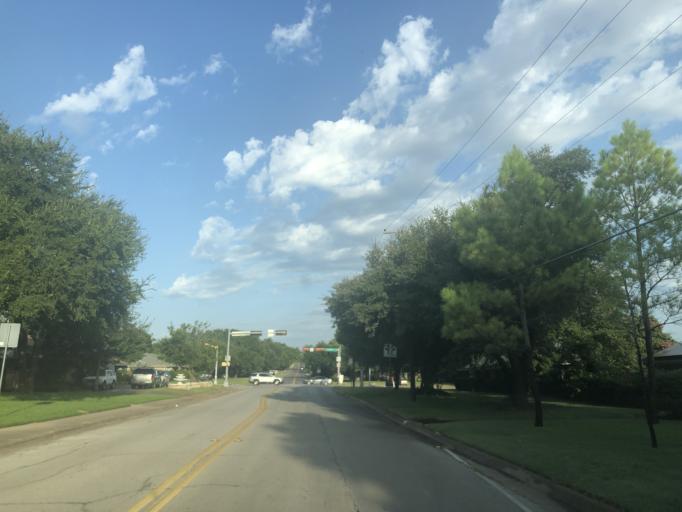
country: US
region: Texas
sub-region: Dallas County
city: Grand Prairie
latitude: 32.7643
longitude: -97.0188
